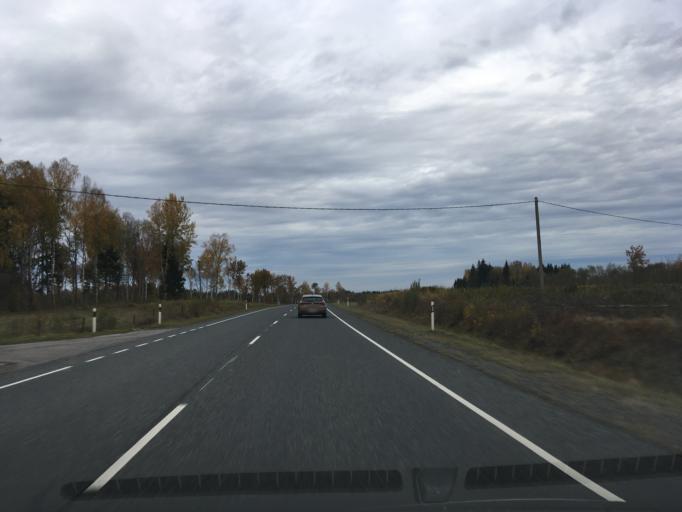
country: EE
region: Harju
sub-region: Nissi vald
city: Turba
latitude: 58.9771
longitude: 24.0587
